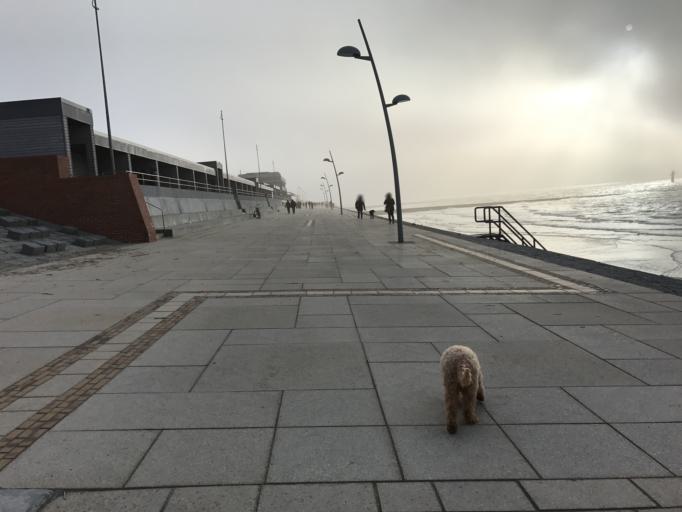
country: DE
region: Lower Saxony
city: Borkum
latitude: 53.5815
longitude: 6.6606
